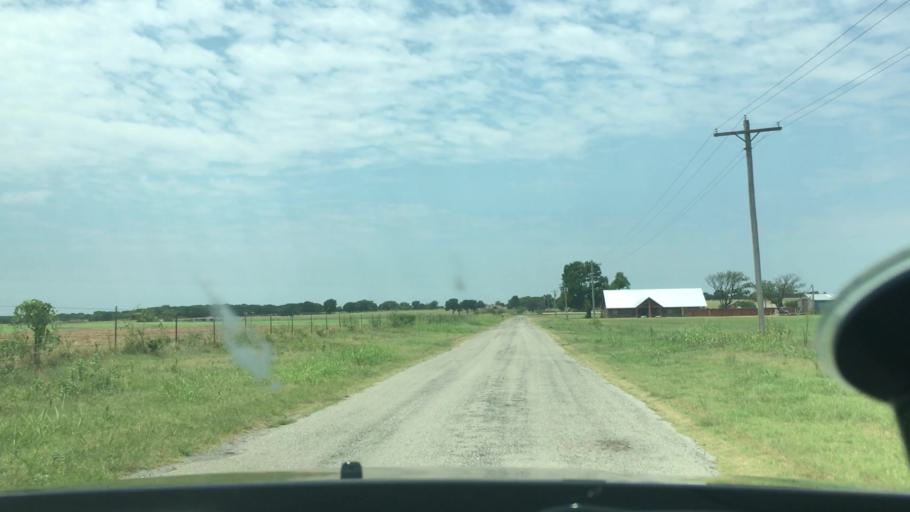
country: US
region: Texas
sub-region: Cooke County
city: Muenster
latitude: 33.8676
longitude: -97.3623
